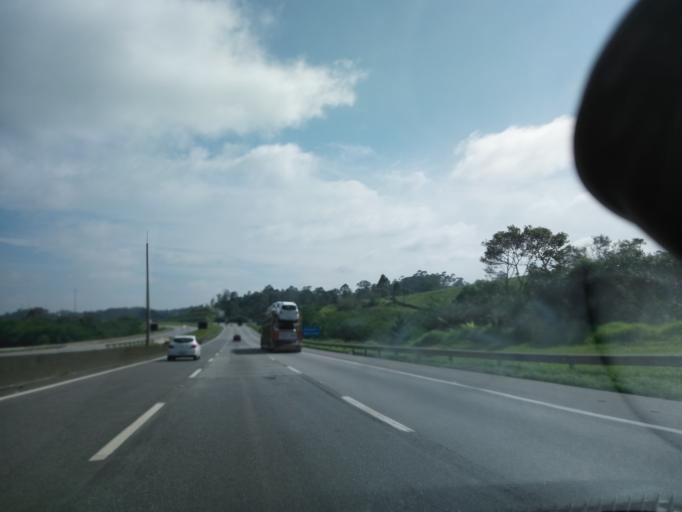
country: BR
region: Sao Paulo
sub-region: Itapecerica Da Serra
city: Itapecerica da Serra
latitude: -23.7321
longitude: -46.8102
